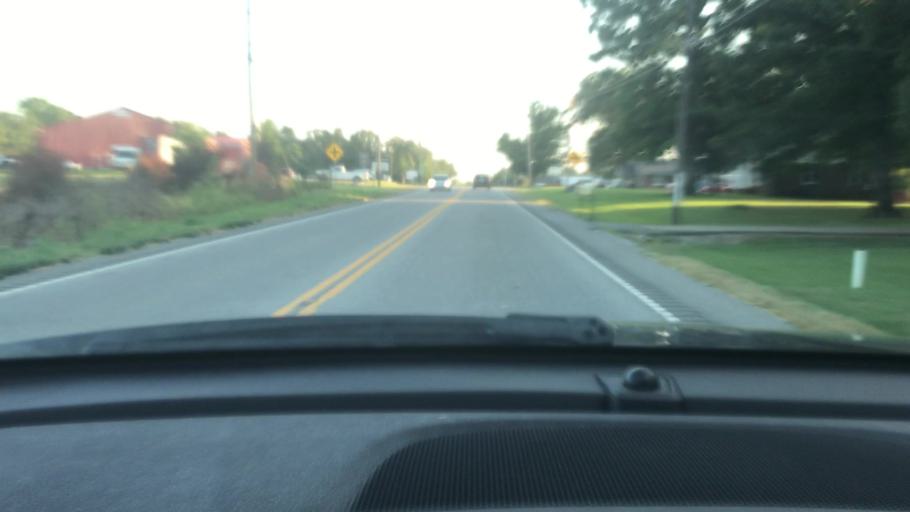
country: US
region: Tennessee
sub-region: Dickson County
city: Dickson
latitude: 36.1090
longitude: -87.3716
